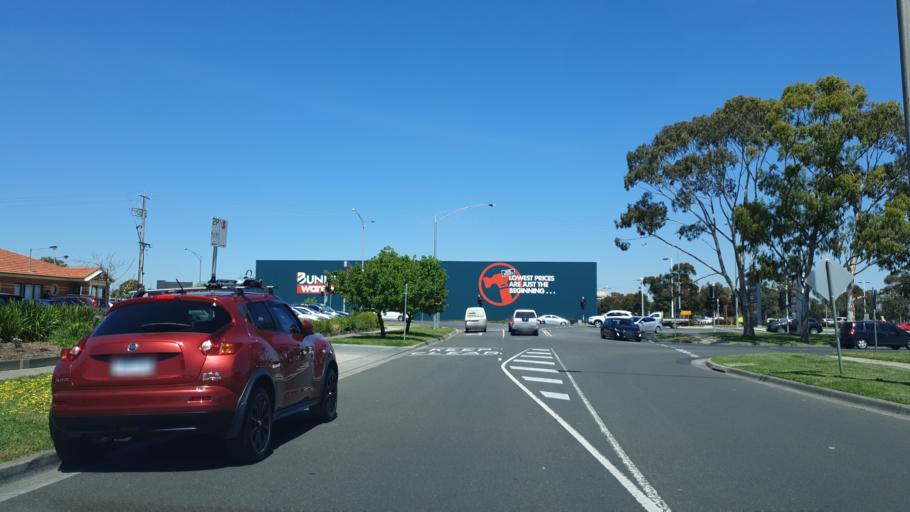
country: AU
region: Victoria
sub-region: Casey
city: Cranbourne North
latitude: -38.0818
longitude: 145.2792
